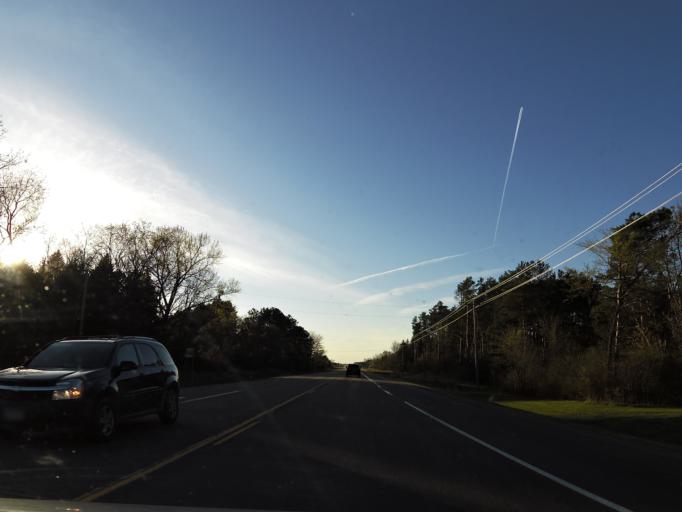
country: US
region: Wisconsin
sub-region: Pierce County
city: Prescott
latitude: 44.6681
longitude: -92.7835
